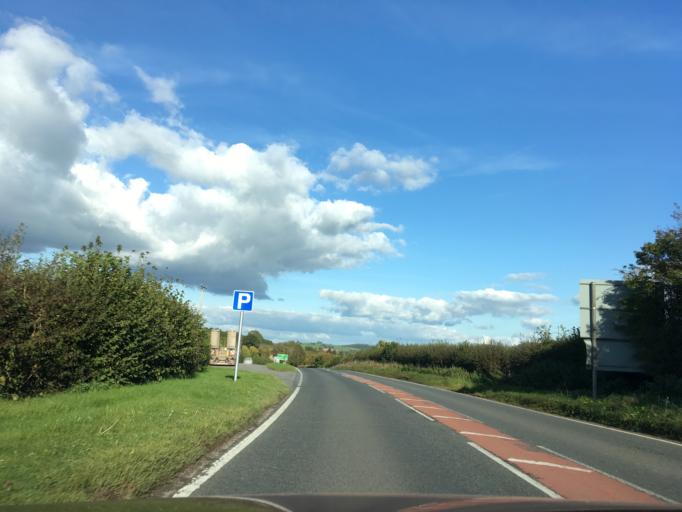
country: GB
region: Wales
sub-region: Sir Powys
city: Hay
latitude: 52.0132
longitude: -3.2379
